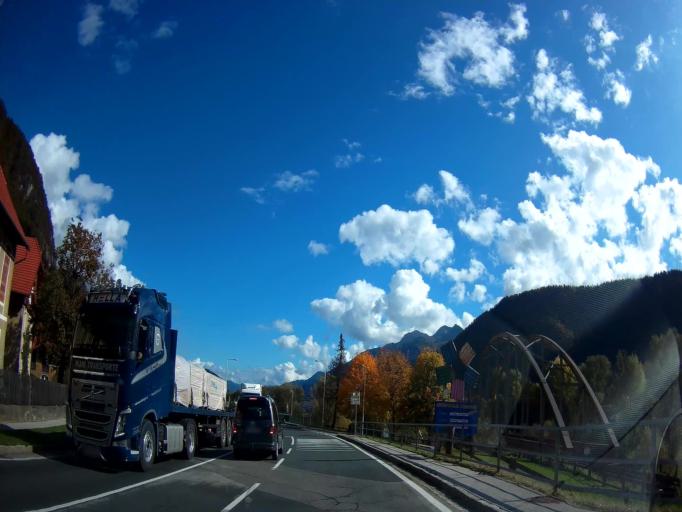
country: AT
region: Carinthia
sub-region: Politischer Bezirk Spittal an der Drau
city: Oberdrauburg
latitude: 46.7478
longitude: 12.9673
